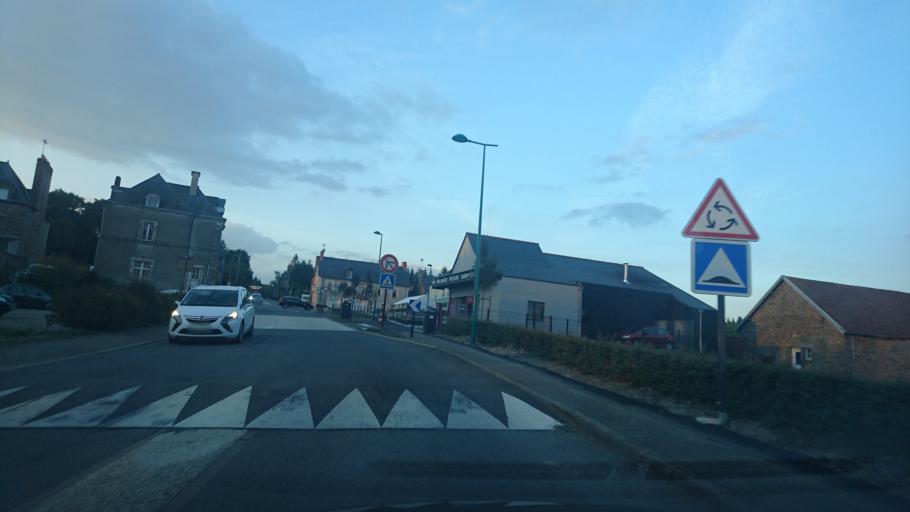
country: FR
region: Brittany
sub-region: Departement d'Ille-et-Vilaine
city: Baulon
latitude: 47.9282
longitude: -1.9418
